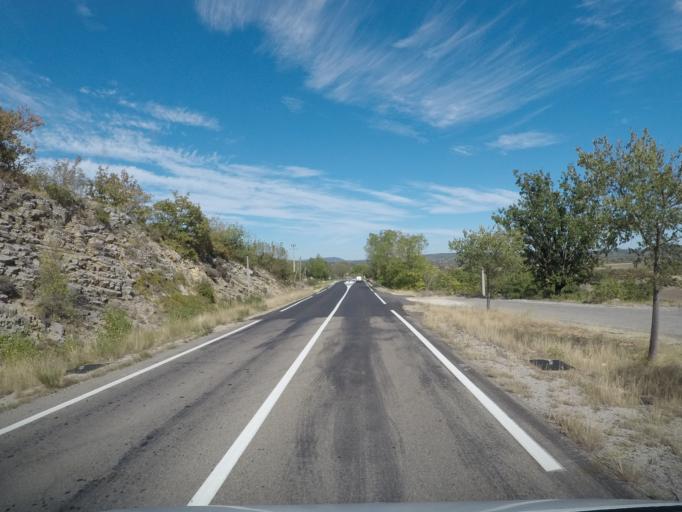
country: FR
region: Languedoc-Roussillon
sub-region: Departement de l'Herault
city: Saint-Martin-de-Londres
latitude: 43.8057
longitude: 3.7391
